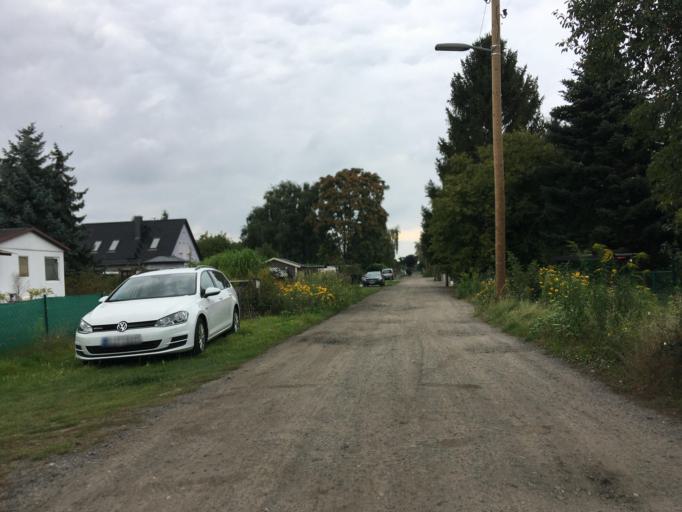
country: DE
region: Berlin
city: Biesdorf
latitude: 52.4882
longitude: 13.5545
